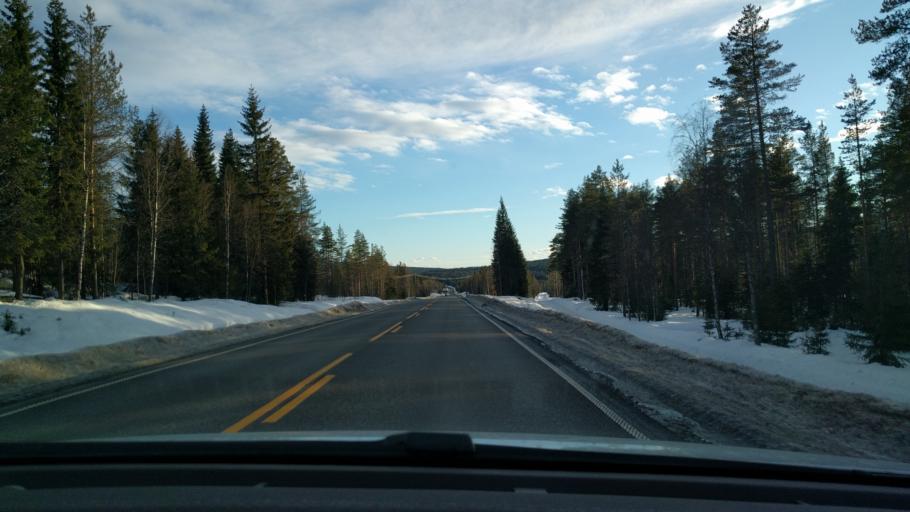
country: NO
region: Hedmark
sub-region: Elverum
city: Elverum
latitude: 61.0420
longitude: 11.8729
